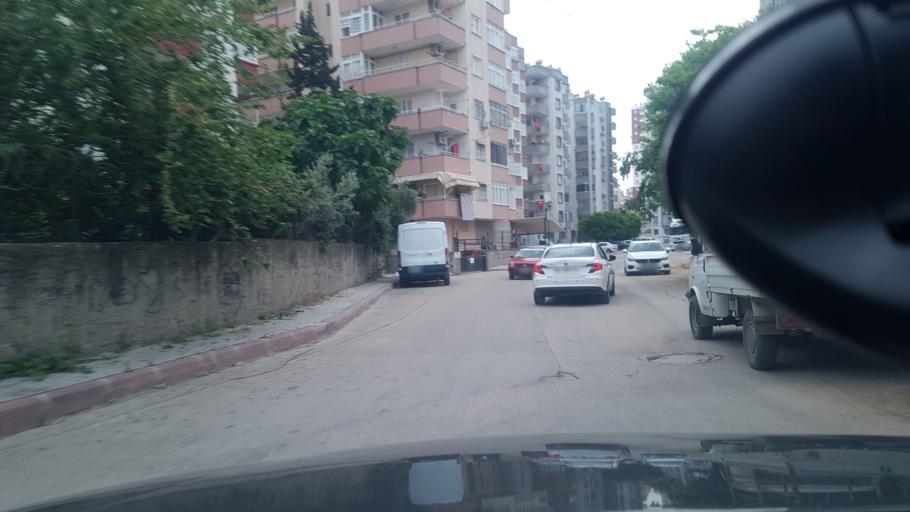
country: TR
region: Adana
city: Seyhan
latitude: 37.0257
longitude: 35.2889
